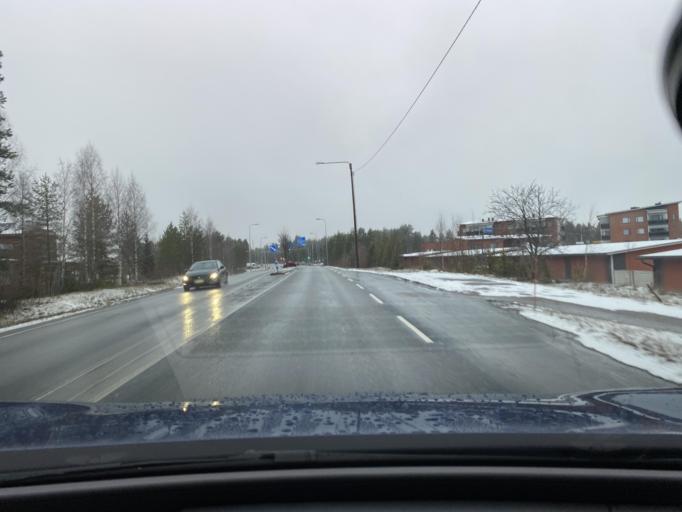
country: FI
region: Northern Ostrobothnia
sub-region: Oulu
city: Kiiminki
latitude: 65.1285
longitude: 25.7810
